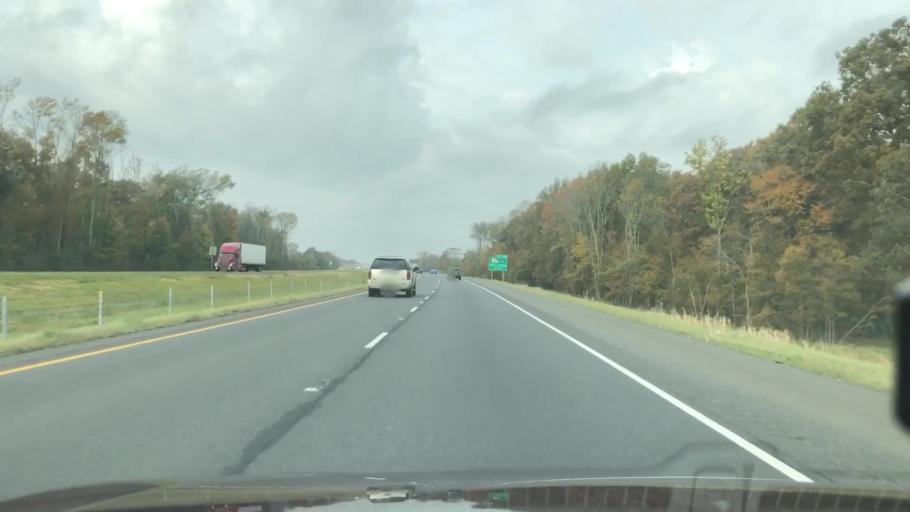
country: US
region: Louisiana
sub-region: Richland Parish
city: Delhi
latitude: 32.4558
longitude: -91.6128
